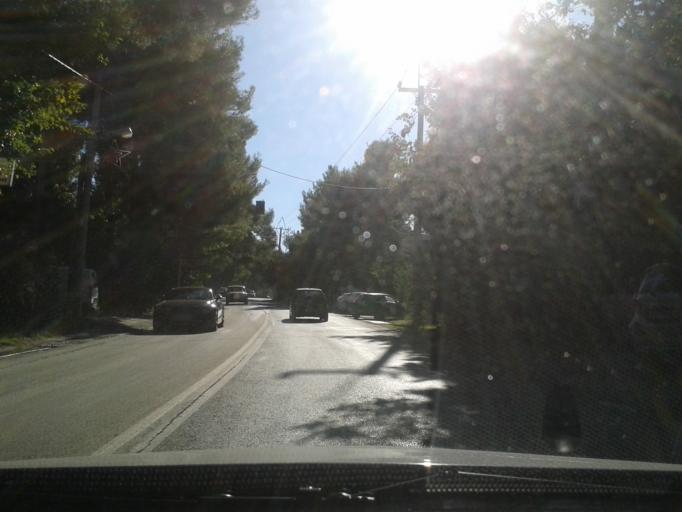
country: GR
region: Attica
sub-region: Nomarchia Anatolikis Attikis
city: Drosia
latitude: 38.1079
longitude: 23.8617
